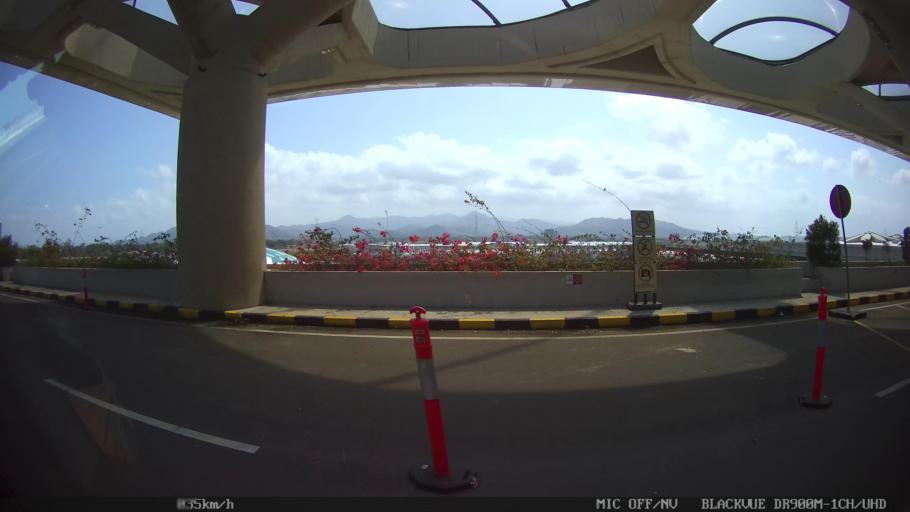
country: ID
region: Daerah Istimewa Yogyakarta
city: Srandakan
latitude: -7.8973
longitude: 110.0599
